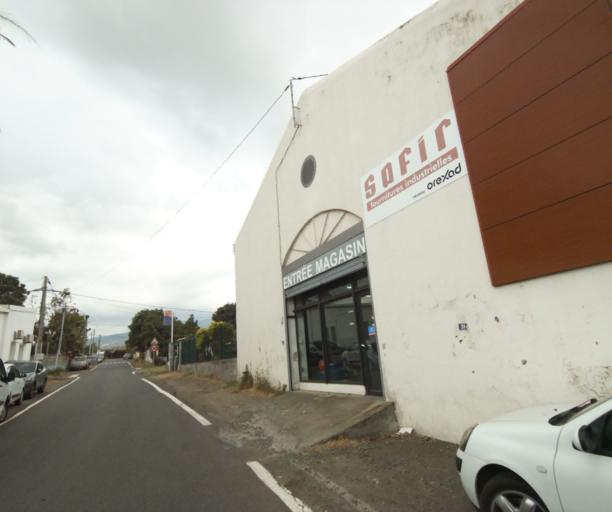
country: RE
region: Reunion
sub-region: Reunion
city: Saint-Paul
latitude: -20.9874
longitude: 55.2987
